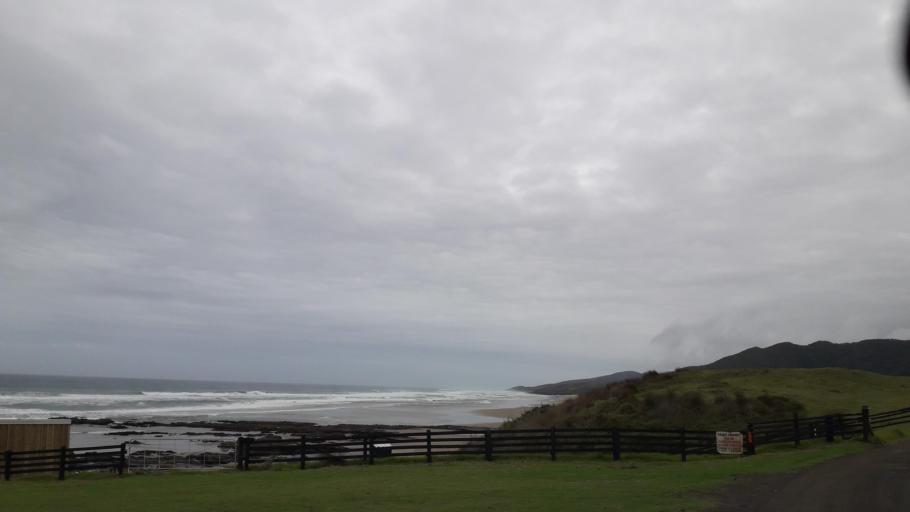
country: NZ
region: Northland
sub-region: Far North District
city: Ahipara
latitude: -35.4288
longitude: 173.2707
